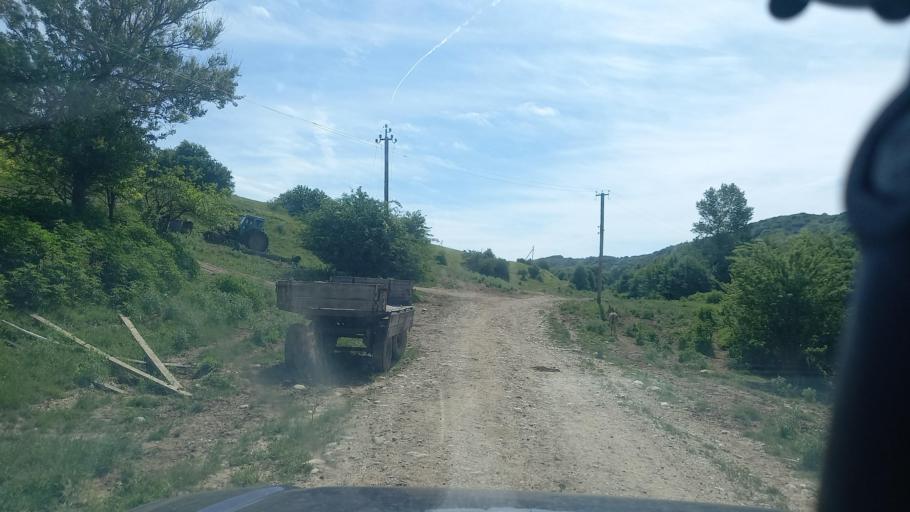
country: RU
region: Karachayevo-Cherkesiya
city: Kurdzhinovo
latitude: 44.1419
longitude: 41.0571
